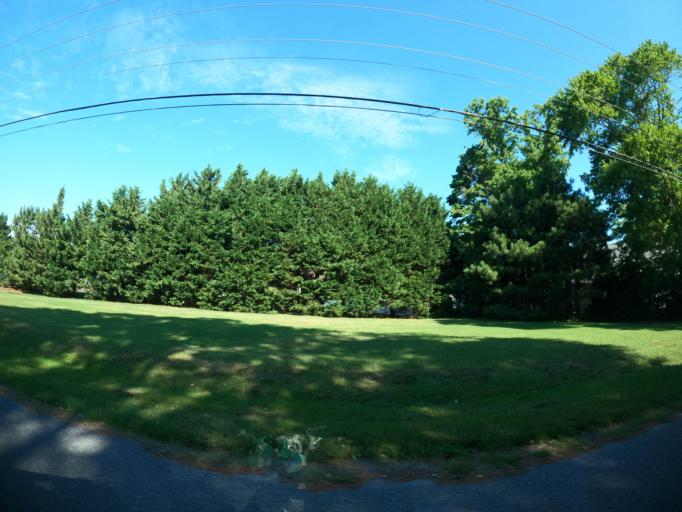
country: US
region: Delaware
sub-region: Sussex County
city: Ocean View
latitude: 38.5268
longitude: -75.0934
